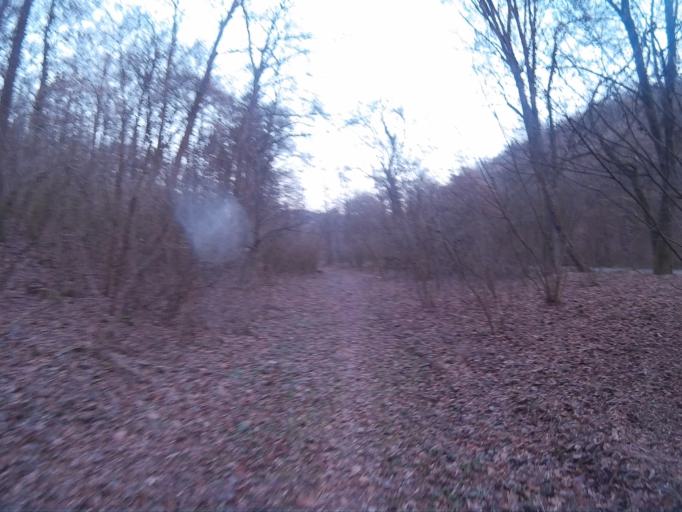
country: HU
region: Borsod-Abauj-Zemplen
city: Putnok
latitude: 48.3222
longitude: 20.4400
